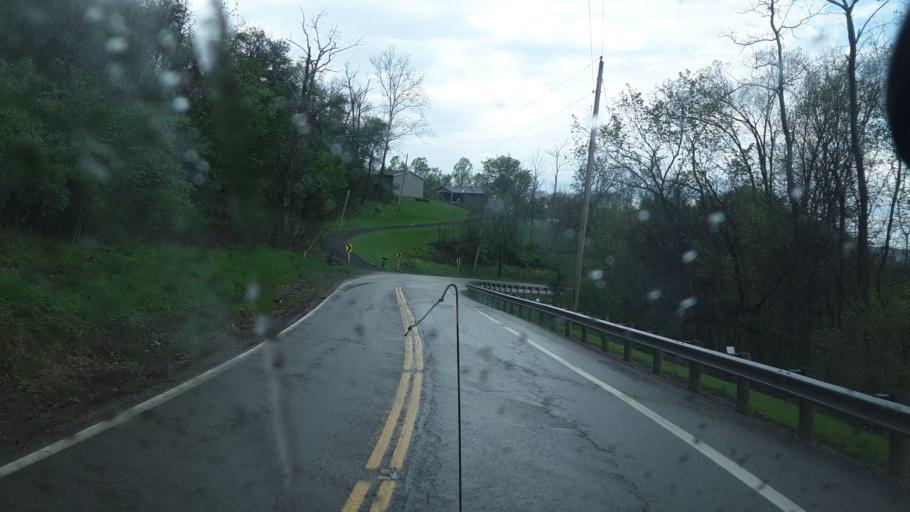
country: US
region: Ohio
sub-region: Muskingum County
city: New Concord
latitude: 40.0571
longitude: -81.7442
